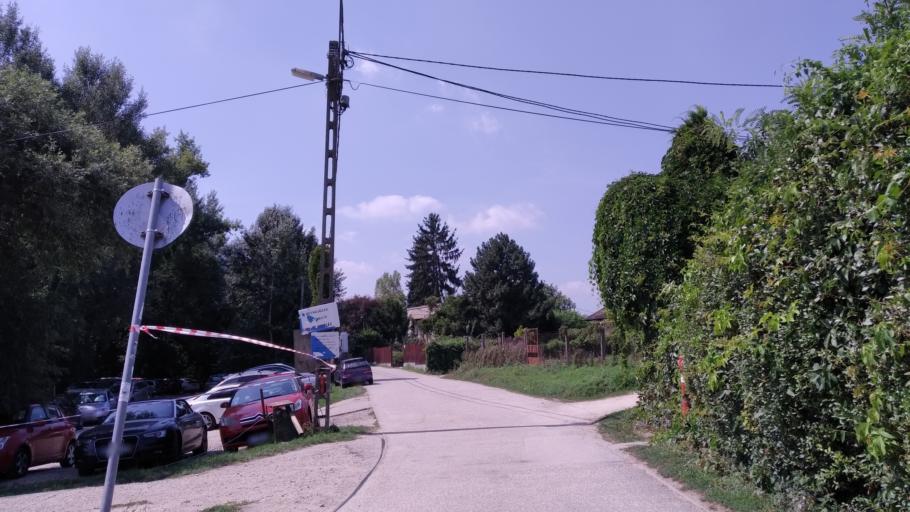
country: HU
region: Pest
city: Budakalasz
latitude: 47.6189
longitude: 19.0841
